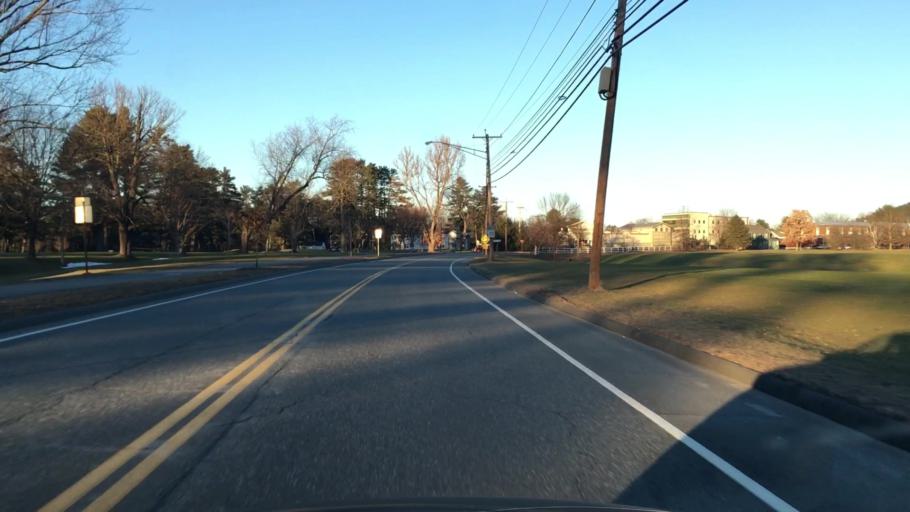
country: US
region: New Hampshire
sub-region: Grafton County
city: Hanover
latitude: 43.7165
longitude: -72.2754
